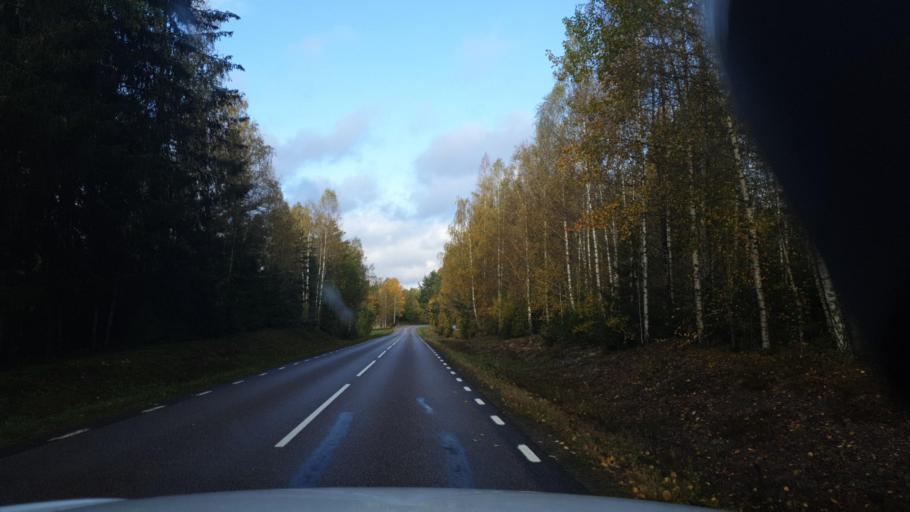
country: SE
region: Vaermland
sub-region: Arvika Kommun
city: Arvika
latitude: 59.5132
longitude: 12.6414
